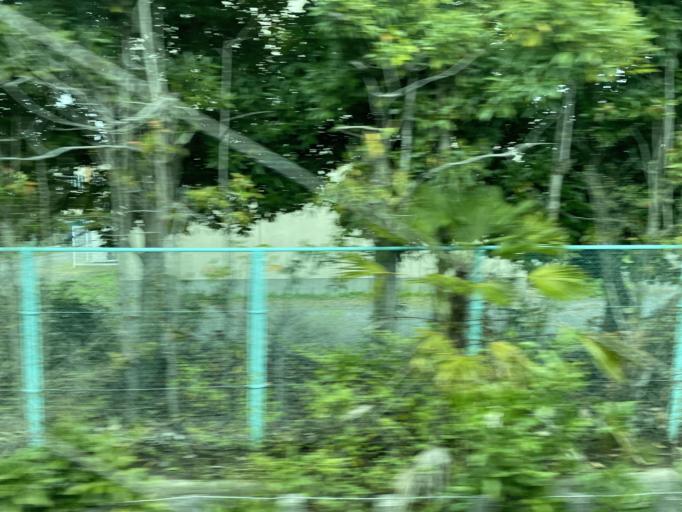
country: JP
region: Saitama
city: Kukichuo
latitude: 36.0531
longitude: 139.6834
